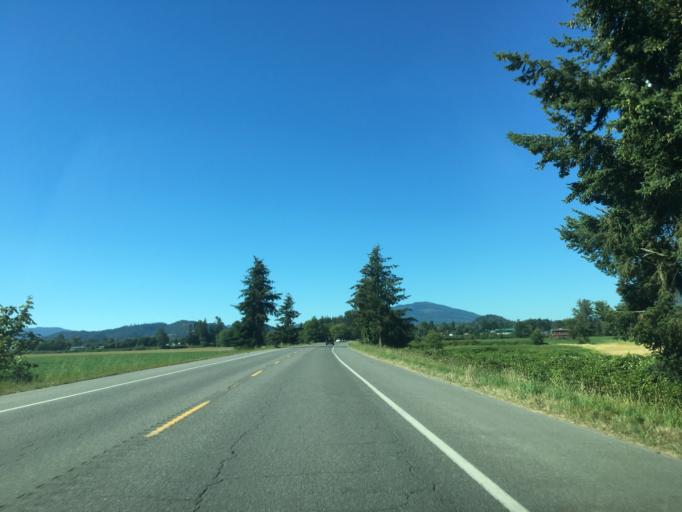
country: US
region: Washington
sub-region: Skagit County
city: Sedro-Woolley
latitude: 48.4903
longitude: -122.2462
